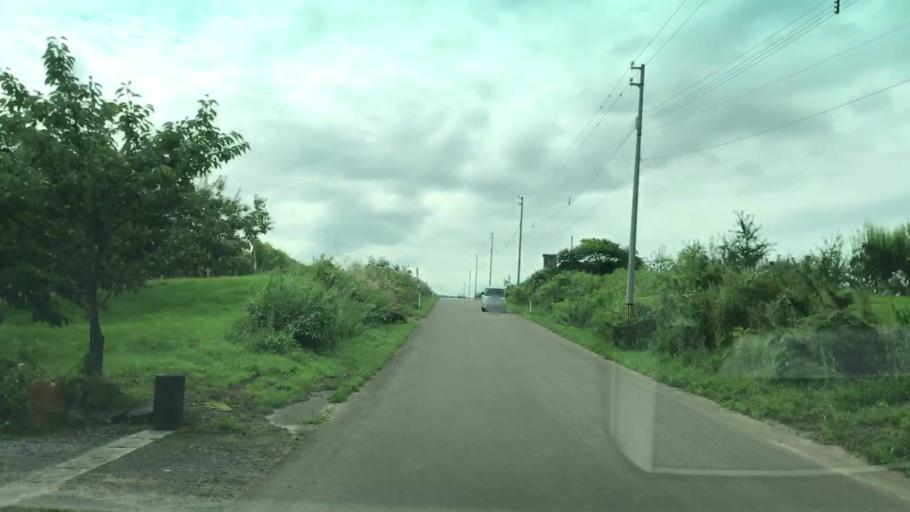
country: JP
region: Hokkaido
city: Yoichi
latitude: 43.1767
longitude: 140.8383
